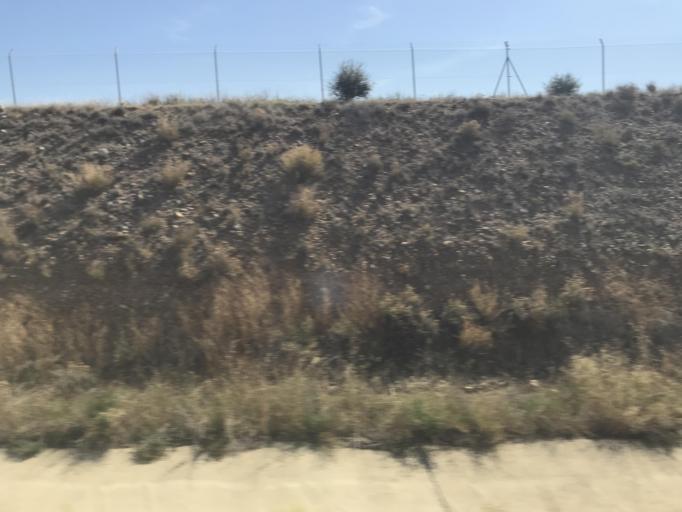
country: ES
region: Aragon
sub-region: Provincia de Zaragoza
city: Urrea de Jalon
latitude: 41.6723
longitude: -1.2693
